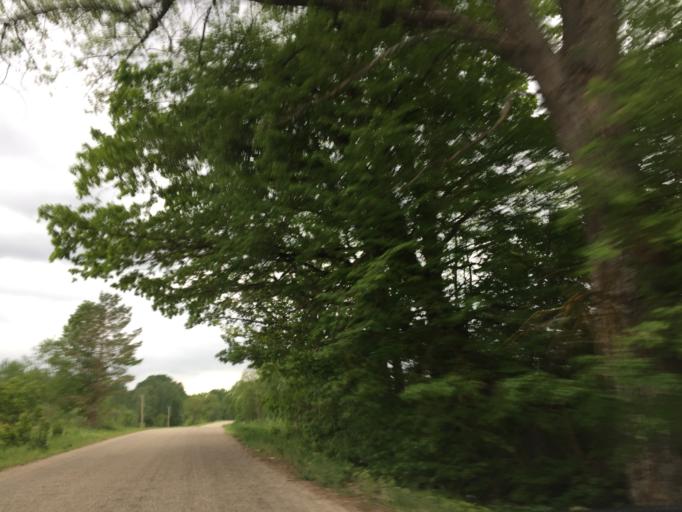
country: LV
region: Aglona
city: Aglona
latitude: 56.0916
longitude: 26.9521
